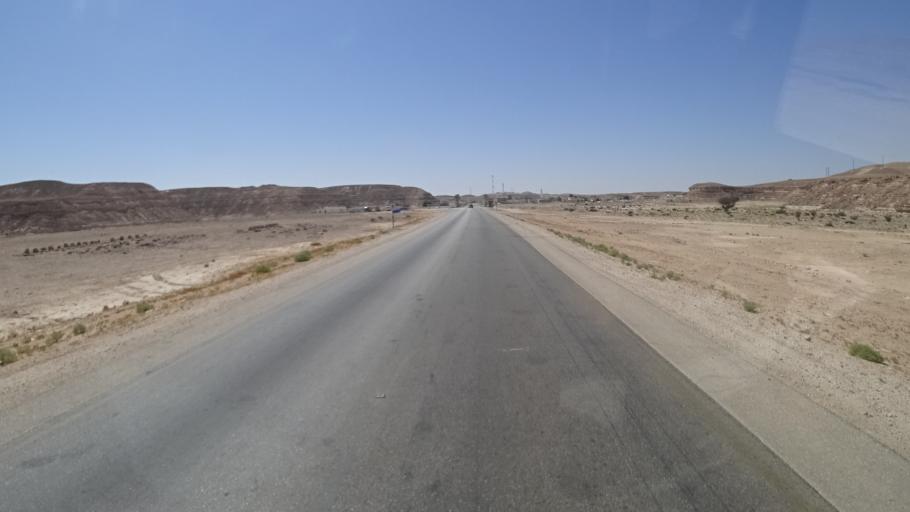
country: OM
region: Zufar
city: Salalah
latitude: 17.4903
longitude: 53.3583
